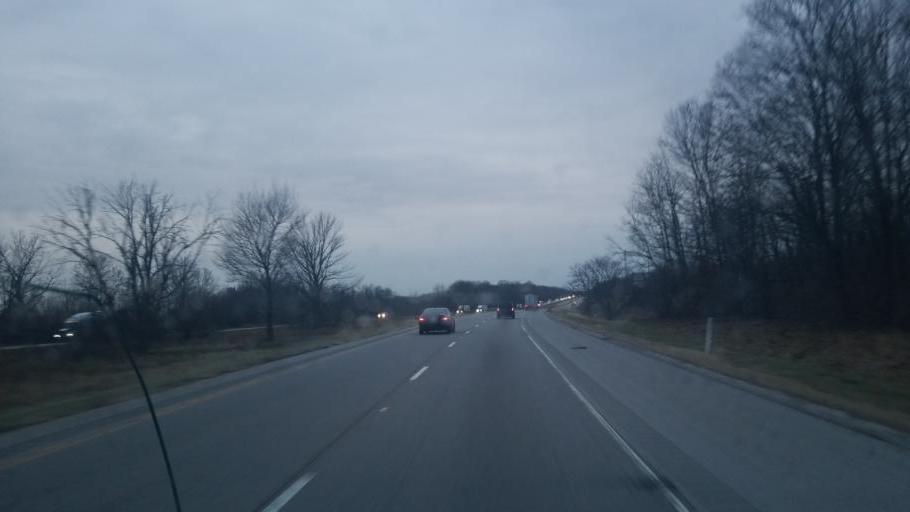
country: US
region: Indiana
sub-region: Vigo County
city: Seelyville
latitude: 39.4462
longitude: -87.2113
